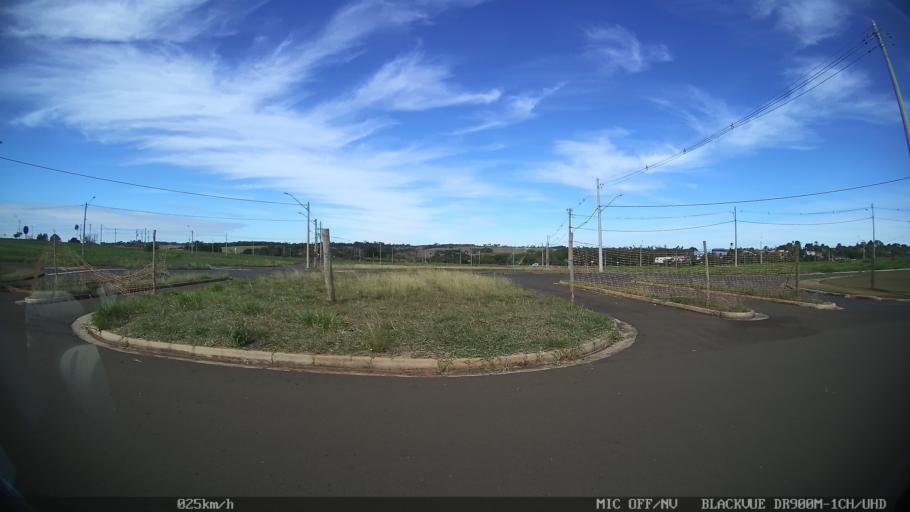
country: BR
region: Sao Paulo
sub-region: Sao Jose Do Rio Preto
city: Sao Jose do Rio Preto
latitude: -20.8568
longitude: -49.3772
